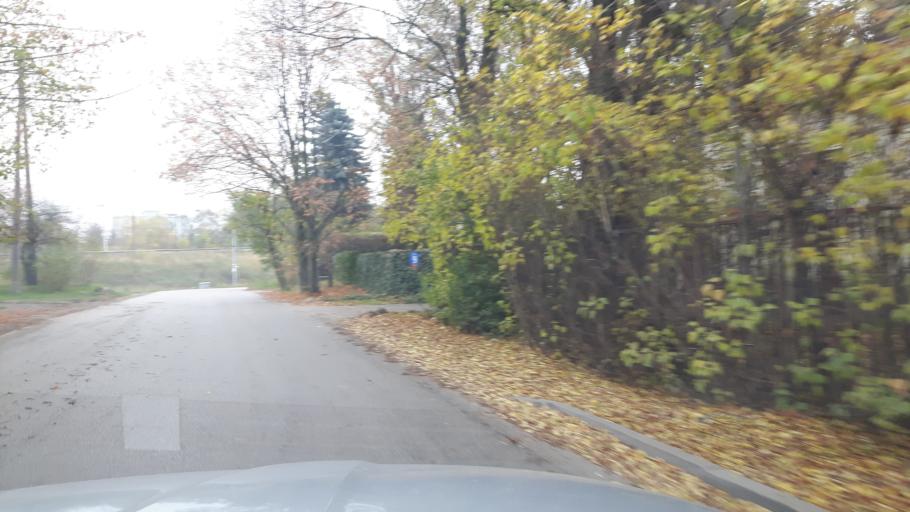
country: PL
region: Masovian Voivodeship
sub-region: Warszawa
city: Wlochy
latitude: 52.2036
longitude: 20.9420
